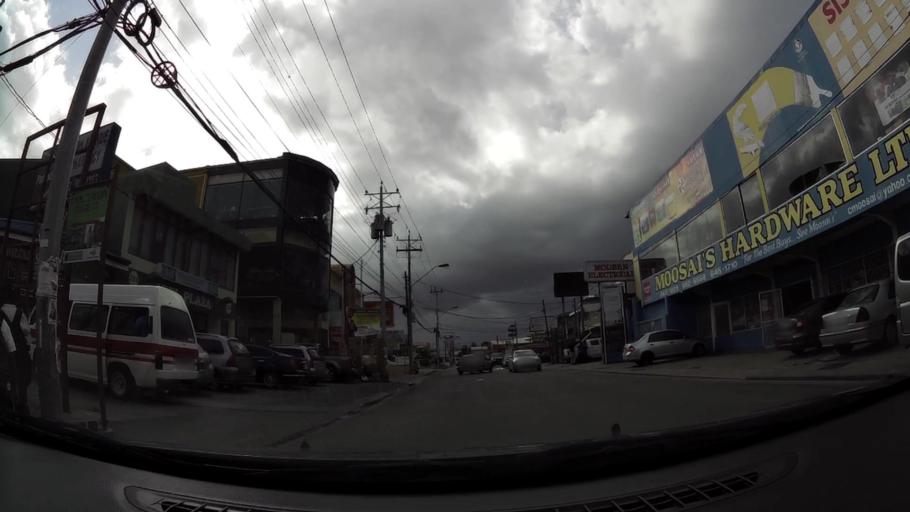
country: TT
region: Tunapuna/Piarco
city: Tunapuna
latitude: 10.6462
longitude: -61.3773
